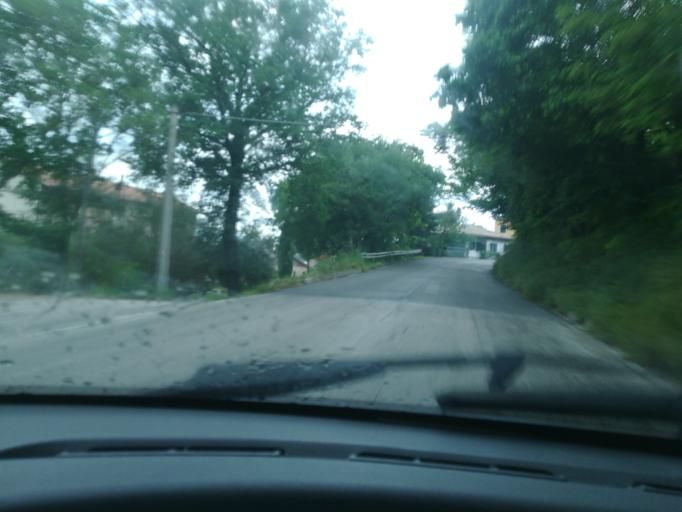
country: IT
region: The Marches
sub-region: Provincia di Macerata
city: Treia
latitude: 43.3064
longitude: 13.3107
